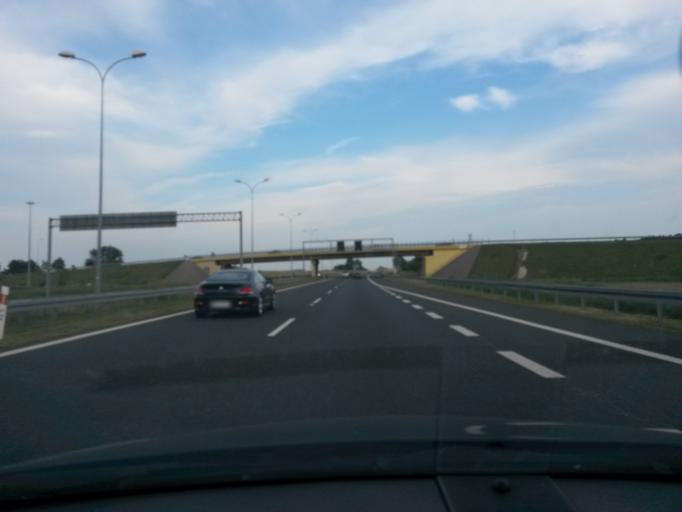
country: PL
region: Lodz Voivodeship
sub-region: Powiat poddebicki
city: Wartkowice
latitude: 51.9937
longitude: 19.0430
